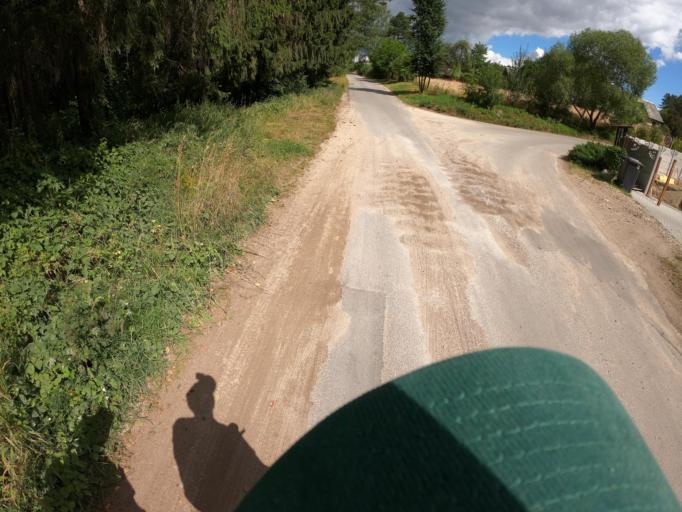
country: LT
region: Alytaus apskritis
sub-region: Alytus
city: Alytus
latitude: 54.4330
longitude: 24.0873
